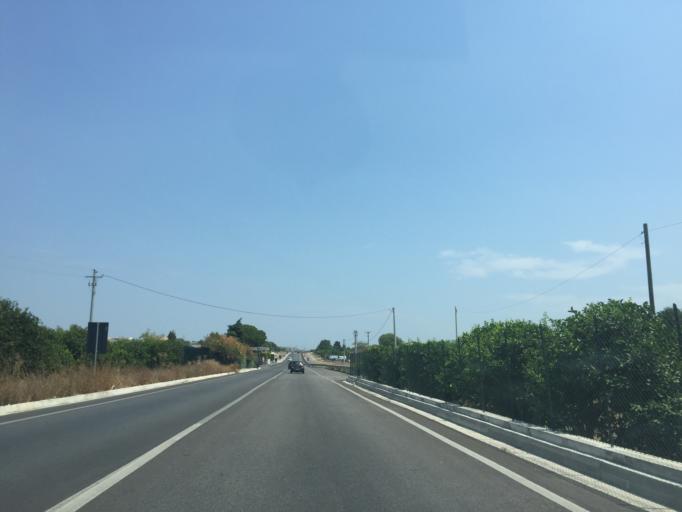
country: IT
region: Sicily
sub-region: Provincia di Siracusa
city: Belvedere
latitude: 37.0719
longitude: 15.2291
